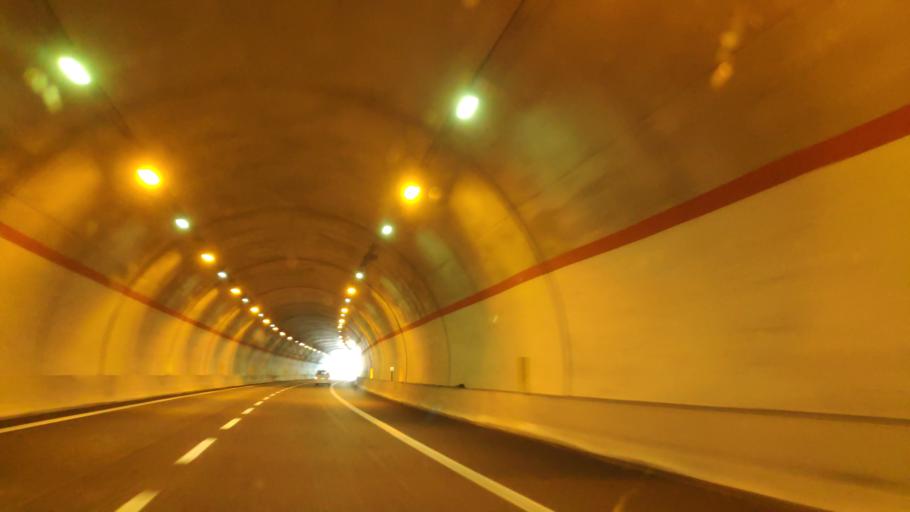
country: IT
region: Calabria
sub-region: Provincia di Cosenza
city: Morano Calabro
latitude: 39.8660
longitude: 16.0808
